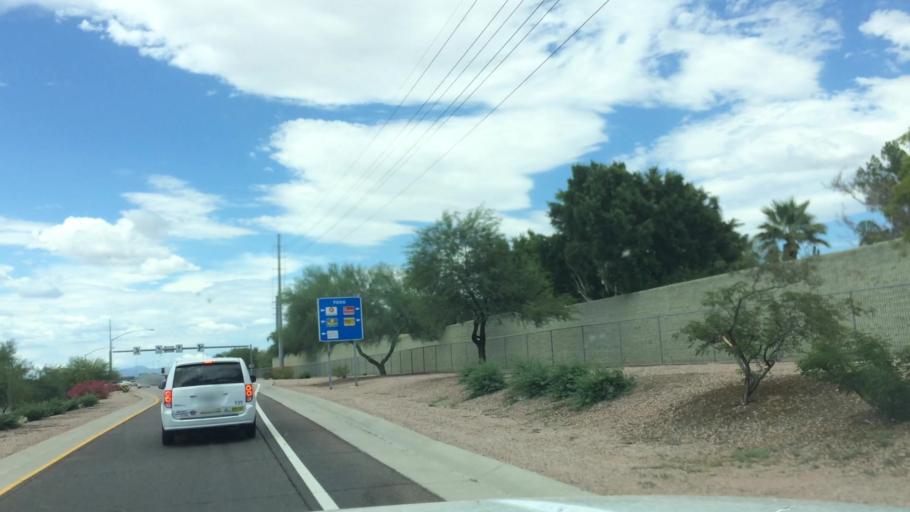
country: US
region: Arizona
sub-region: Maricopa County
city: Paradise Valley
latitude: 33.6159
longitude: -111.8909
